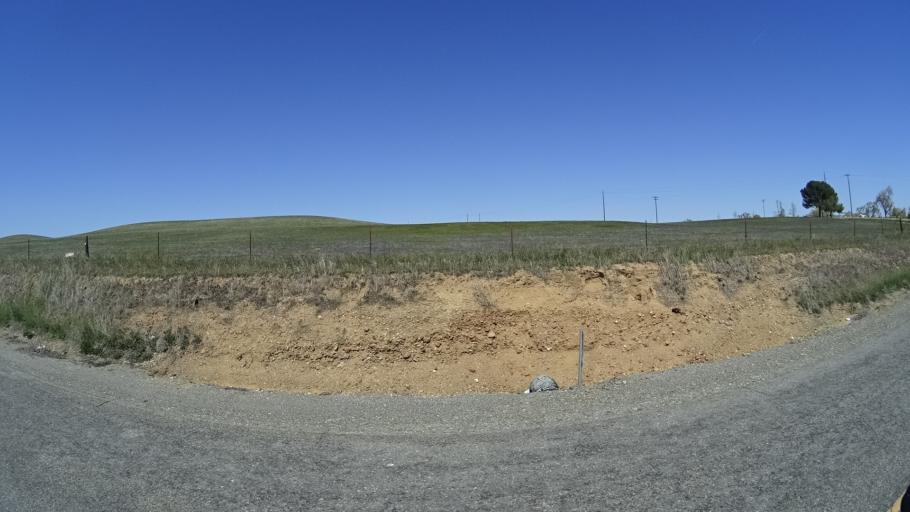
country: US
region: California
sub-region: Glenn County
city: Orland
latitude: 39.7811
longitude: -122.2964
